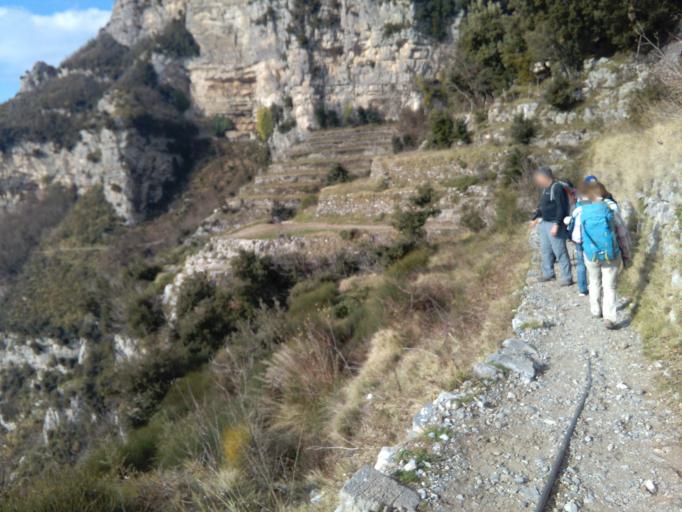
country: IT
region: Campania
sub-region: Provincia di Napoli
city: Agerola
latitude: 40.6250
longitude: 14.5316
